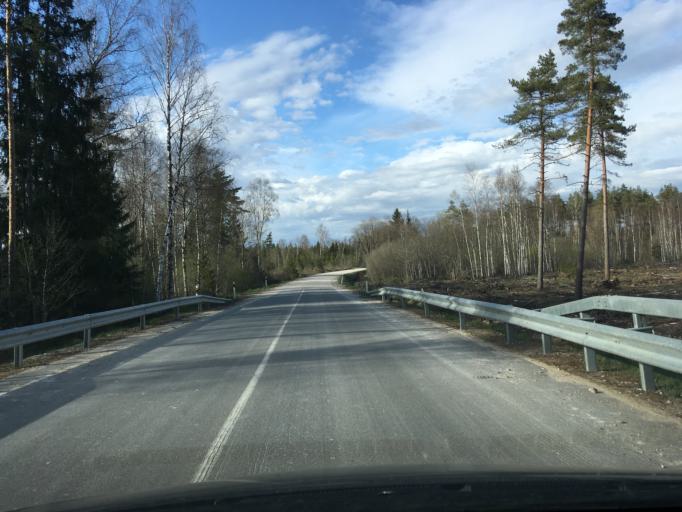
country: EE
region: Raplamaa
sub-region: Maerjamaa vald
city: Marjamaa
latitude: 58.9932
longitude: 24.3673
